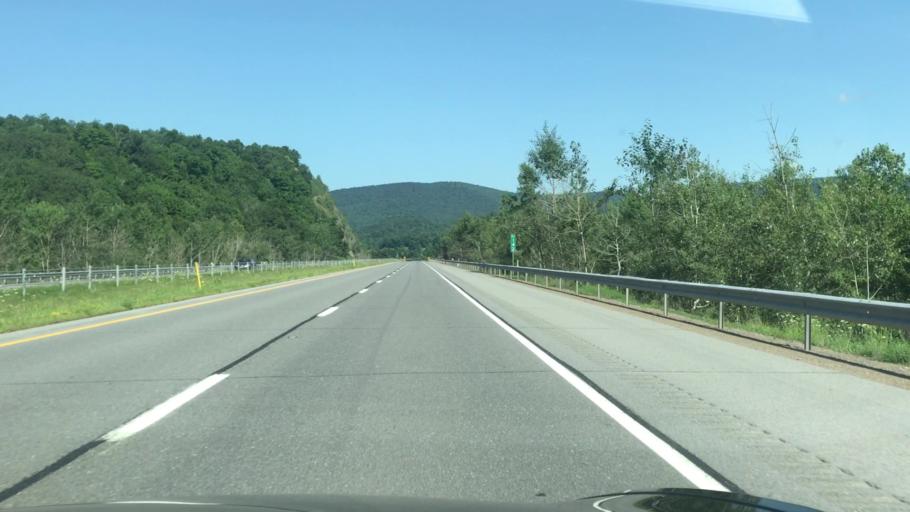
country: US
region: Pennsylvania
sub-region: Lycoming County
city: Garden View
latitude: 41.3127
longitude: -77.0871
